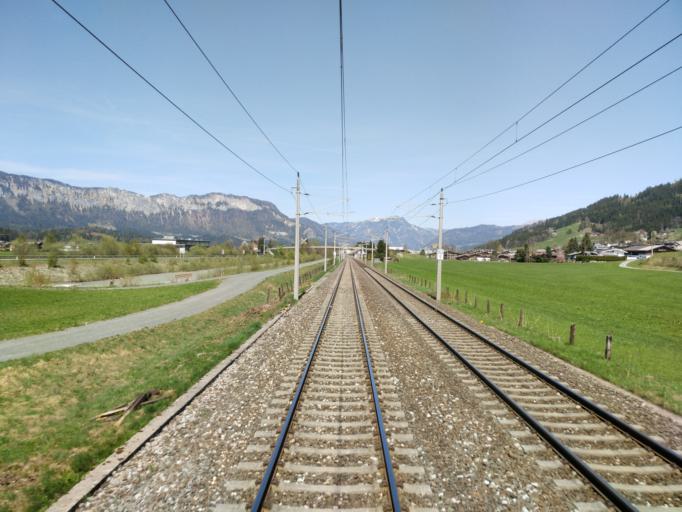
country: AT
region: Tyrol
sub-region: Politischer Bezirk Kitzbuhel
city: Oberndorf in Tirol
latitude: 47.4921
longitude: 12.3864
